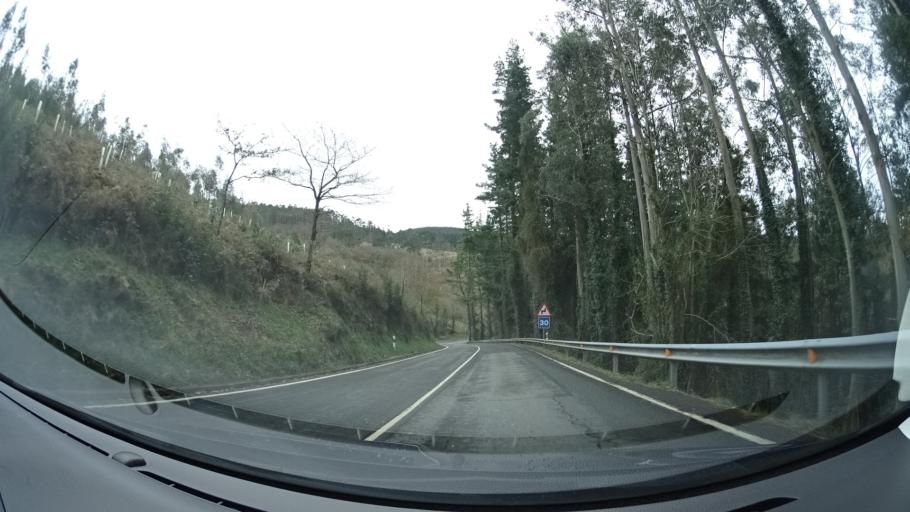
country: ES
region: Basque Country
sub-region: Bizkaia
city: Bakio
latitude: 43.3904
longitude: -2.7693
